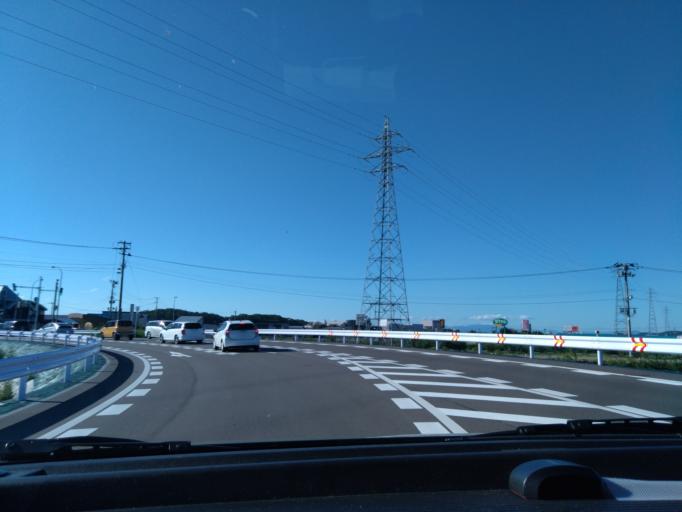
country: JP
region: Akita
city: Yokotemachi
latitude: 39.2907
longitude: 140.5538
